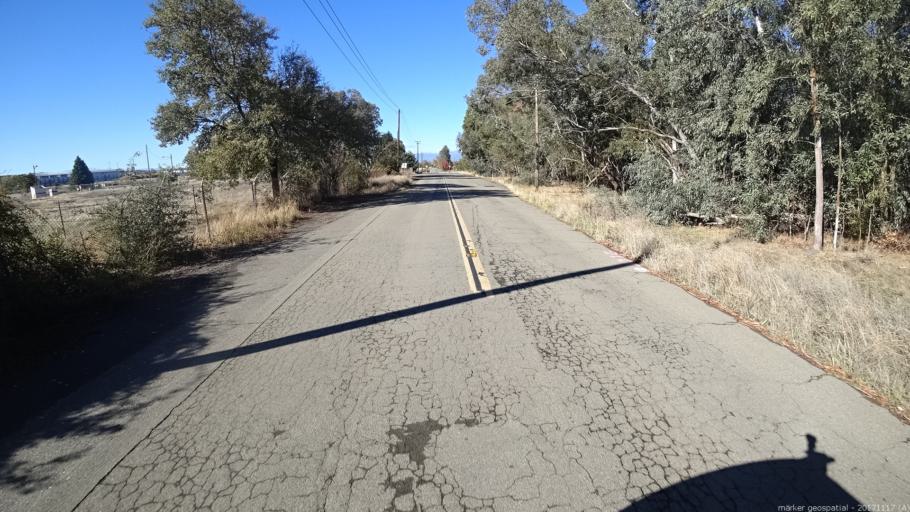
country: US
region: California
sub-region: Shasta County
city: Anderson
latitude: 40.4379
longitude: -122.2684
